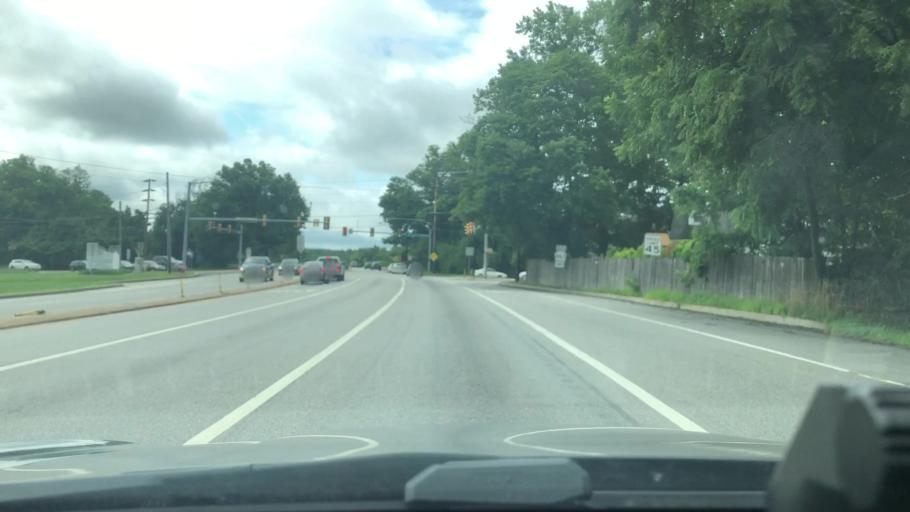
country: US
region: Pennsylvania
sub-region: Montgomery County
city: Pottstown
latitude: 40.2498
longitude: -75.6616
